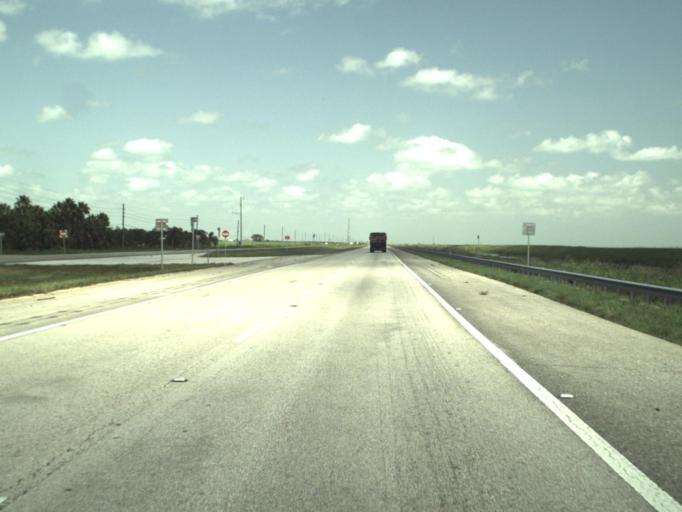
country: US
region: Florida
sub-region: Palm Beach County
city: Belle Glade Camp
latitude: 26.4894
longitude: -80.6573
